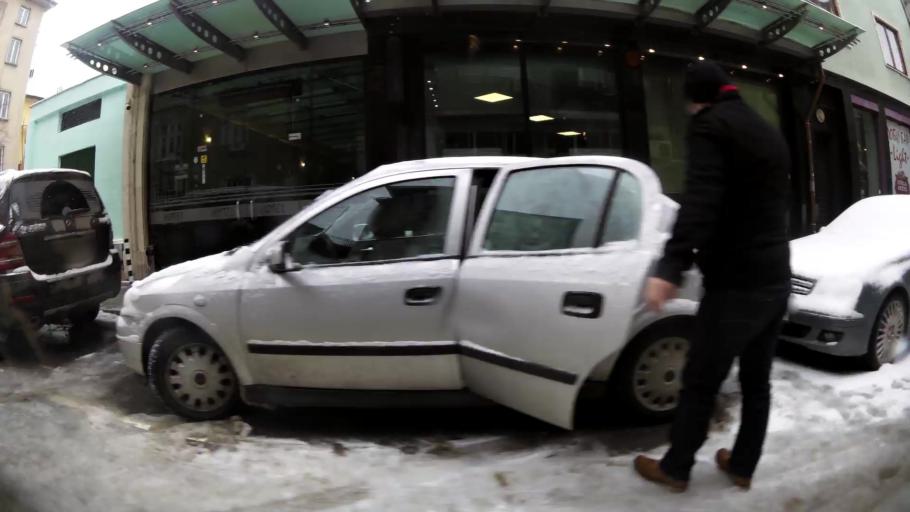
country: BG
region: Sofia-Capital
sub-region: Stolichna Obshtina
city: Sofia
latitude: 42.7030
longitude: 23.3252
